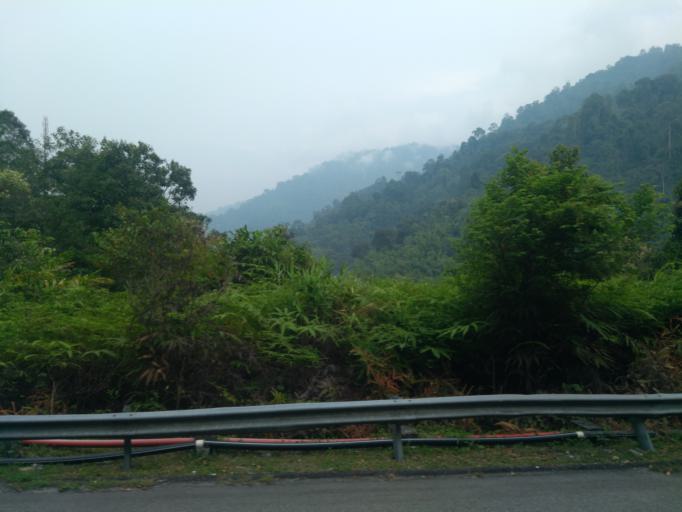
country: MY
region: Pahang
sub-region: Cameron Highlands
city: Tanah Rata
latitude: 4.5735
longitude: 101.2609
